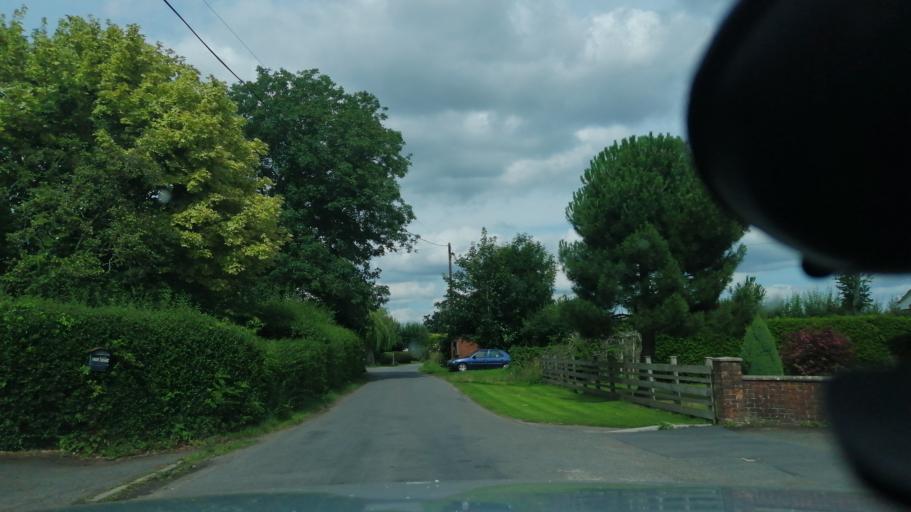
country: GB
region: England
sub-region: Herefordshire
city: Thruxton
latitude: 52.0164
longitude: -2.7966
